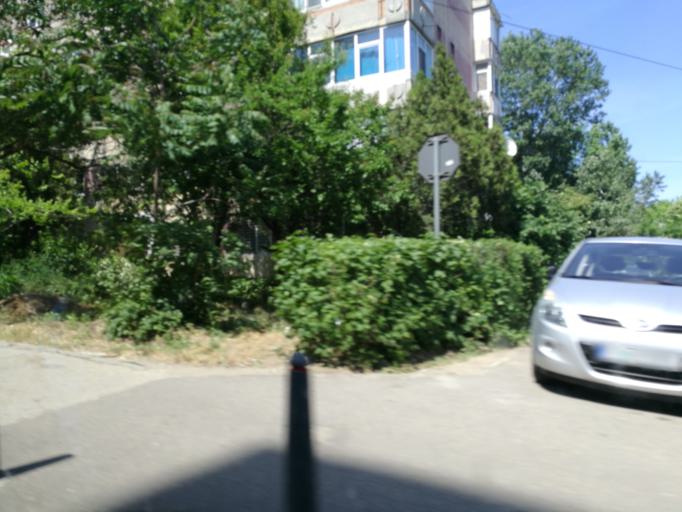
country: RO
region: Constanta
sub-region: Municipiul Constanta
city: Constanta
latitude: 44.2031
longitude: 28.6271
